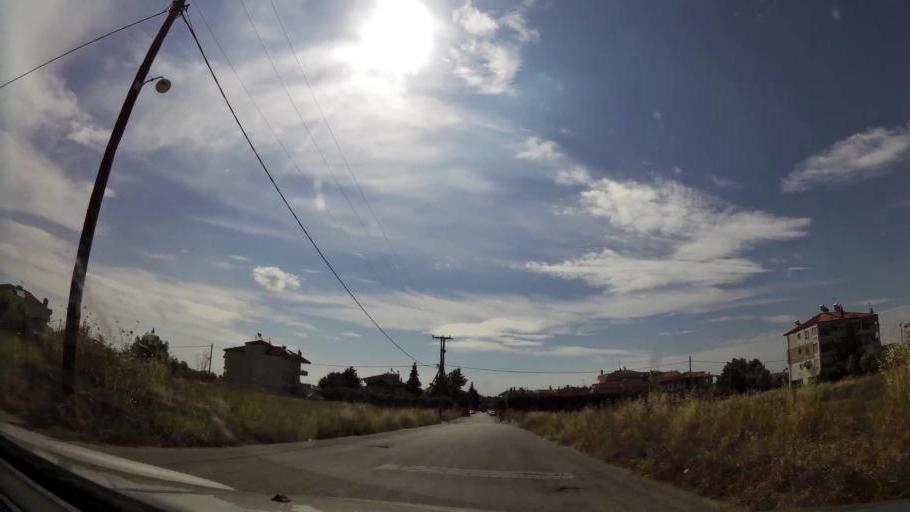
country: GR
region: Central Macedonia
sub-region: Nomos Pierias
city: Katerini
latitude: 40.2818
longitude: 22.4955
